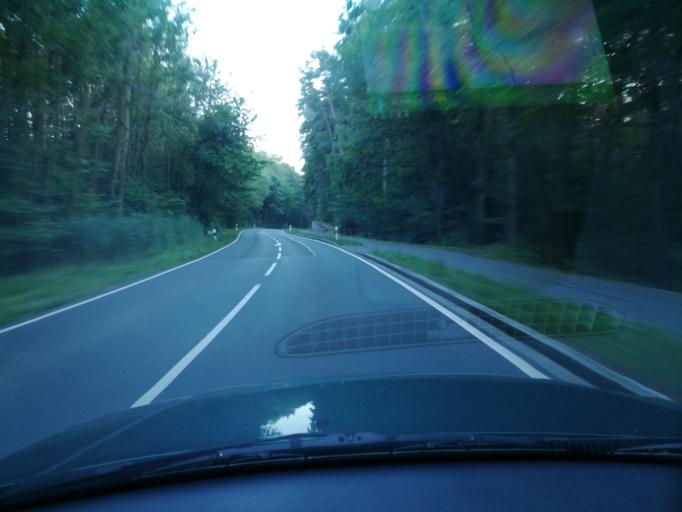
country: DE
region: Bavaria
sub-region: Regierungsbezirk Mittelfranken
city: Hessdorf
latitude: 49.6013
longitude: 10.8969
